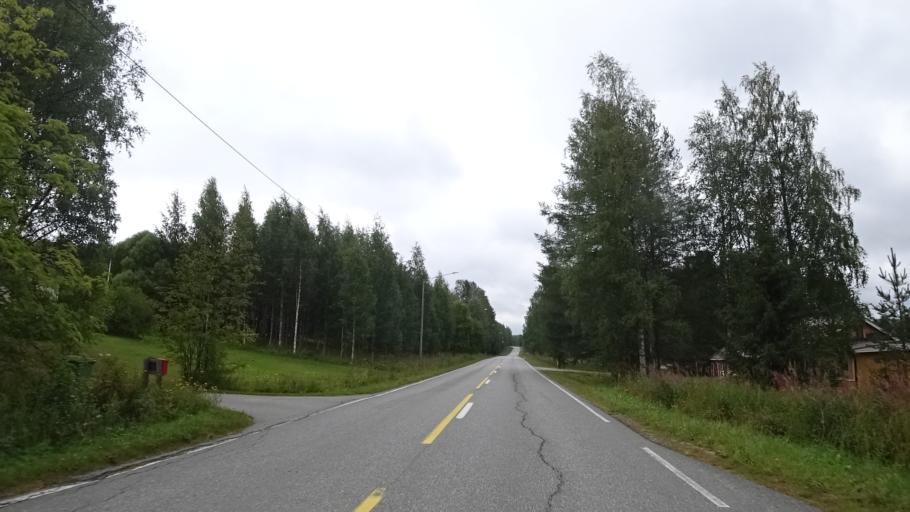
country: FI
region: North Karelia
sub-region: Pielisen Karjala
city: Lieksa
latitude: 63.2835
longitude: 30.5329
